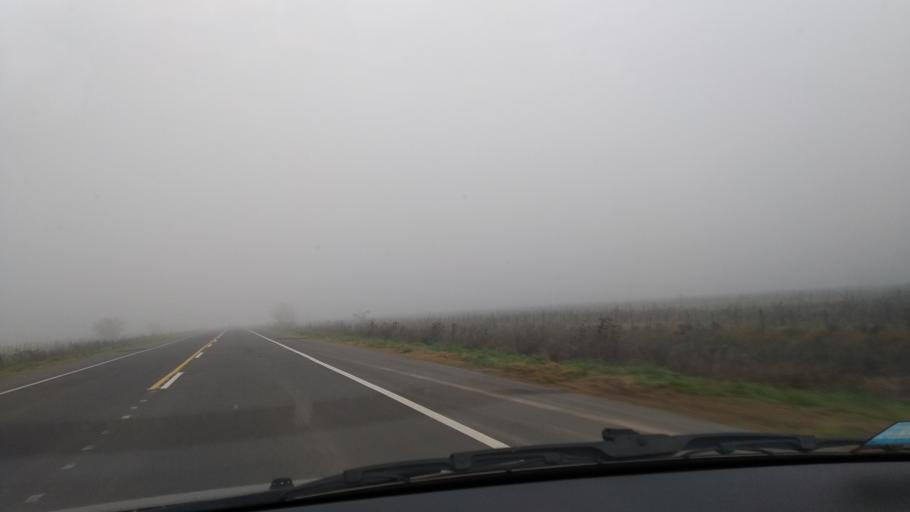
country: AR
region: Buenos Aires
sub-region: Partido de Brandsen
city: Brandsen
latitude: -35.1934
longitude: -58.3707
